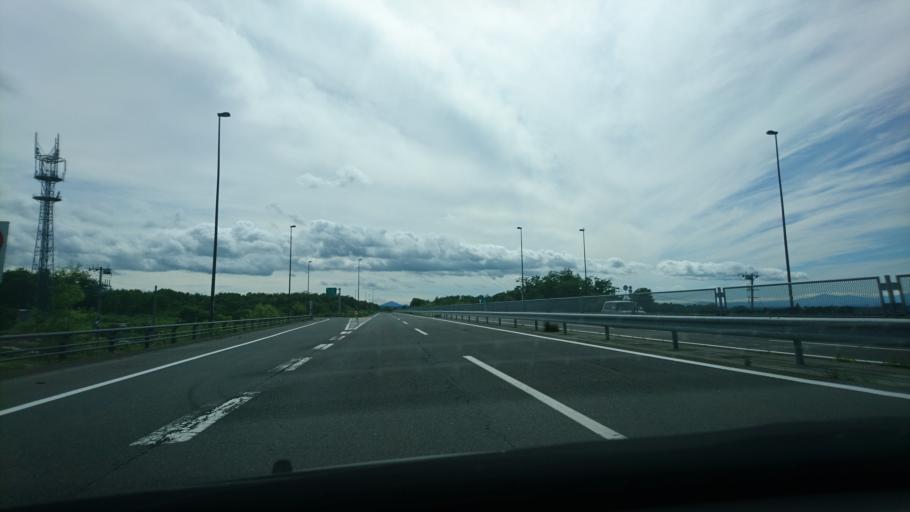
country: JP
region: Aomori
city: Hachinohe
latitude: 40.4822
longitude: 141.5588
